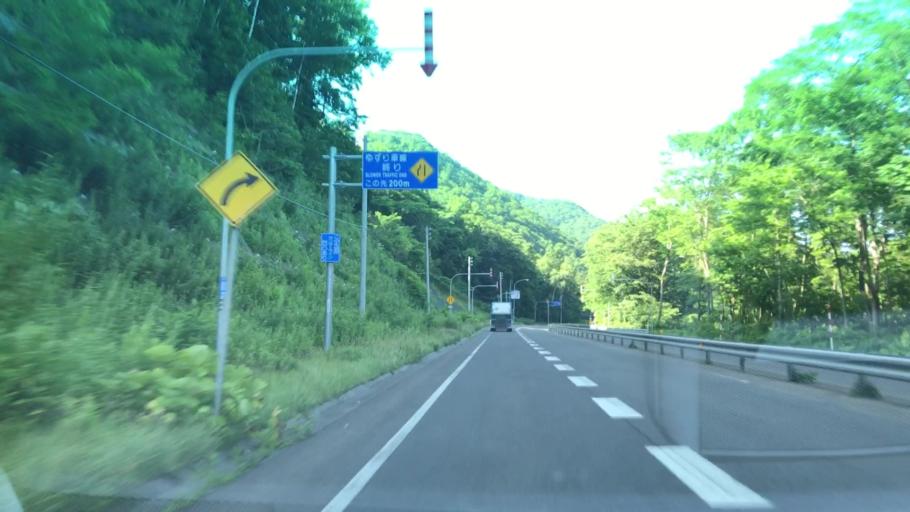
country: JP
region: Hokkaido
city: Iwanai
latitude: 43.0164
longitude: 140.6663
